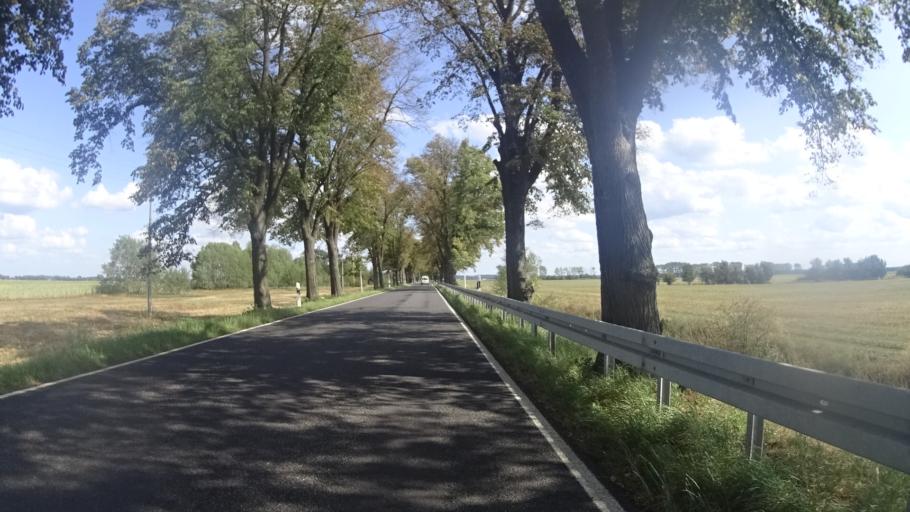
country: DE
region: Brandenburg
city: Rhinow
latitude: 52.7699
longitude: 12.2688
